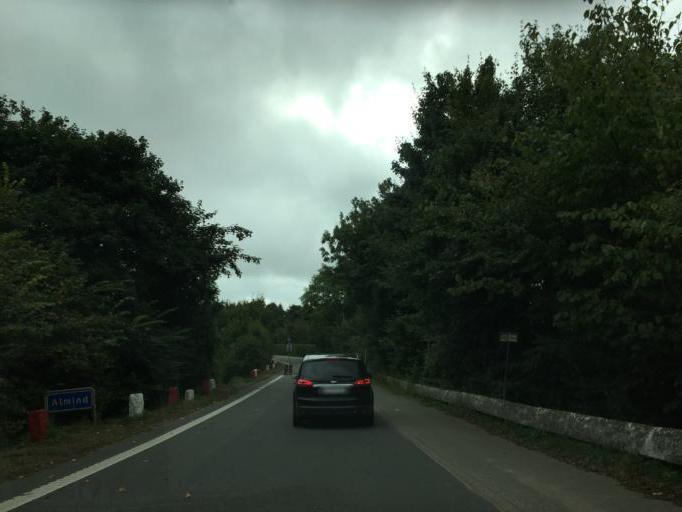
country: DK
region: South Denmark
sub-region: Kolding Kommune
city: Kolding
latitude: 55.5683
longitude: 9.4876
